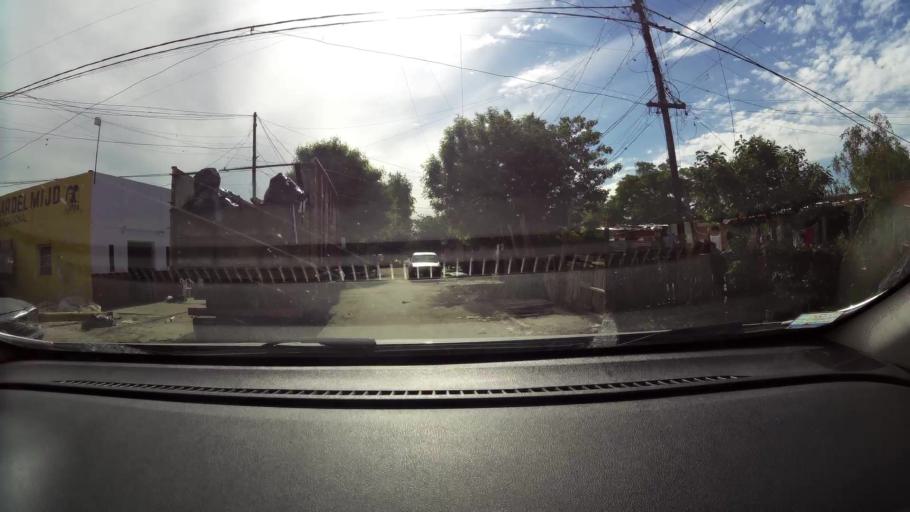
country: AR
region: Santa Fe
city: Granadero Baigorria
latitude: -32.9101
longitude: -60.7049
